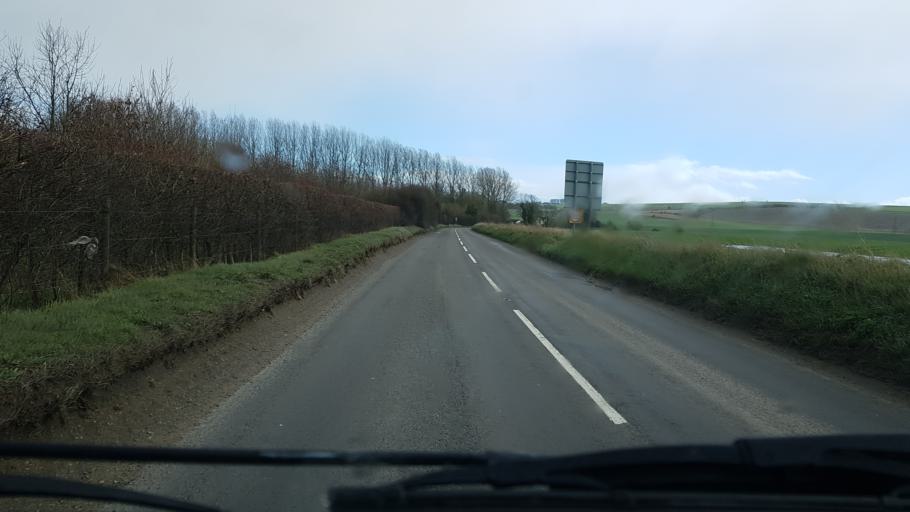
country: GB
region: England
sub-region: Wiltshire
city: Wilsford
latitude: 51.3144
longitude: -1.9121
